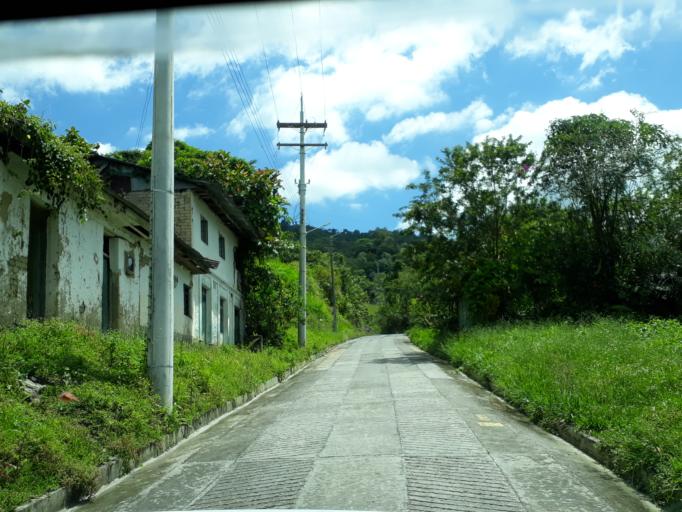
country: CO
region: Cundinamarca
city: Topaipi
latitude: 5.3254
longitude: -74.2140
